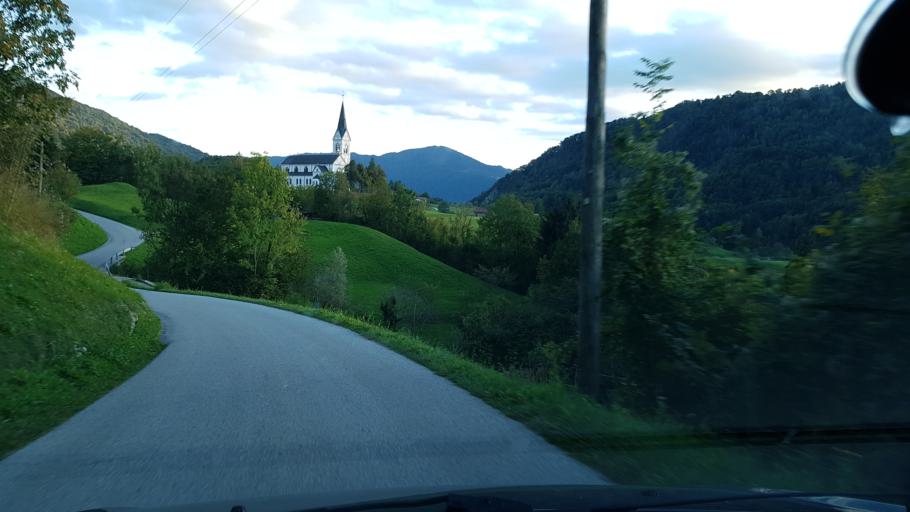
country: SI
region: Kobarid
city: Kobarid
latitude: 46.2610
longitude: 13.6119
